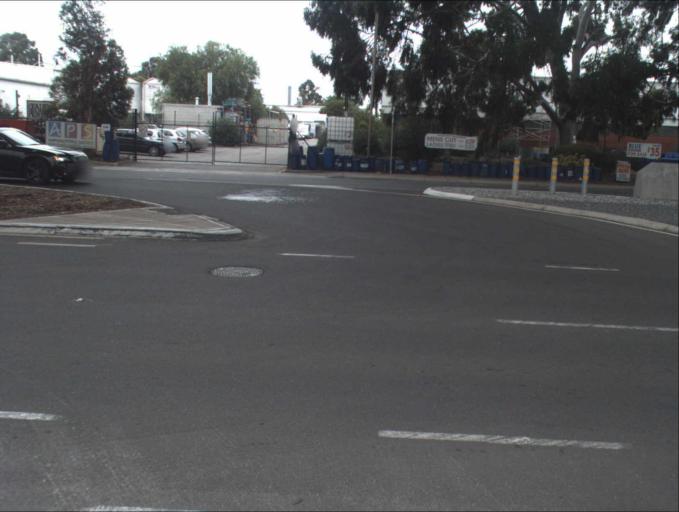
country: AU
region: South Australia
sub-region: Charles Sturt
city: Woodville North
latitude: -34.8552
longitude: 138.5647
